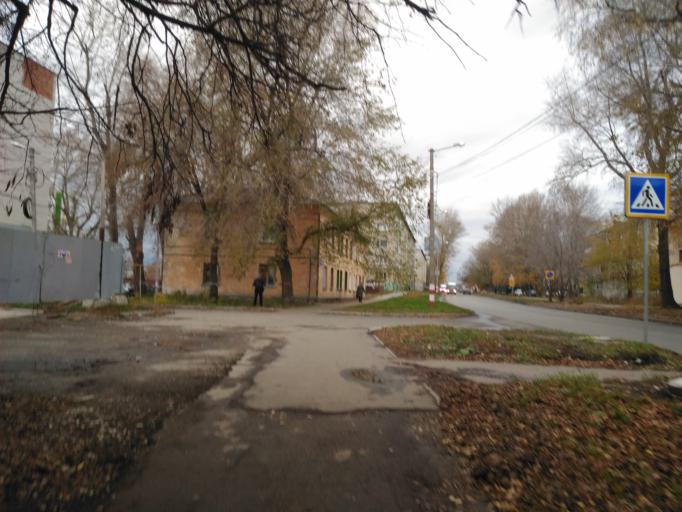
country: RU
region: Ulyanovsk
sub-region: Ulyanovskiy Rayon
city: Ulyanovsk
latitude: 54.3406
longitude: 48.3919
